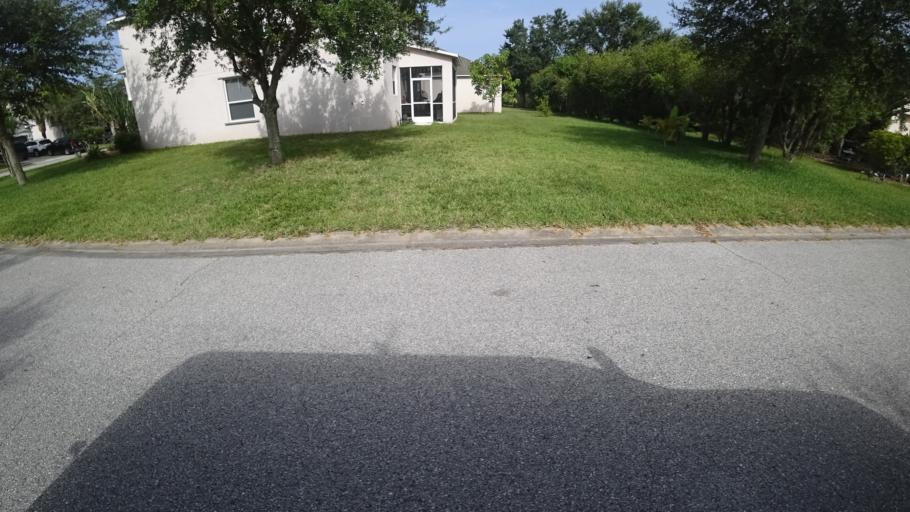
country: US
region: Florida
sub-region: Manatee County
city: Ellenton
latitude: 27.5563
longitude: -82.5047
